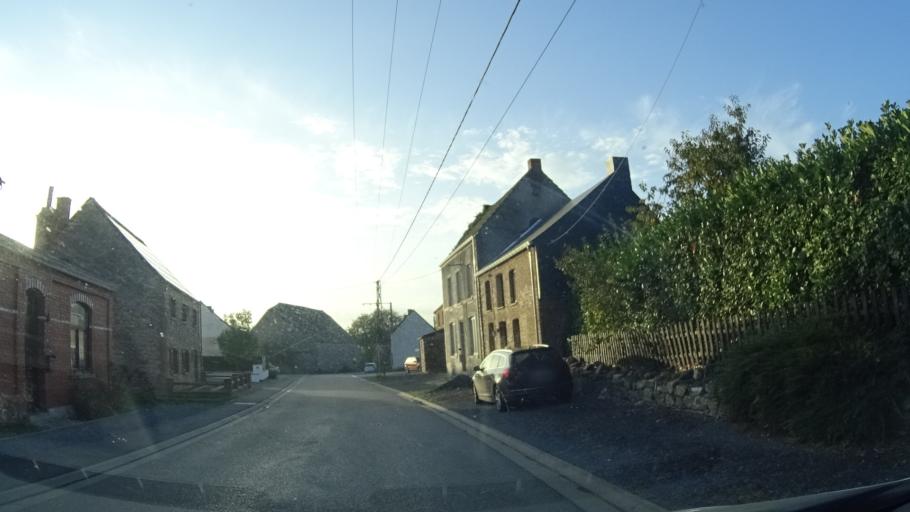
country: BE
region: Wallonia
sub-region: Province du Hainaut
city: Beaumont
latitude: 50.2630
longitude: 4.2305
